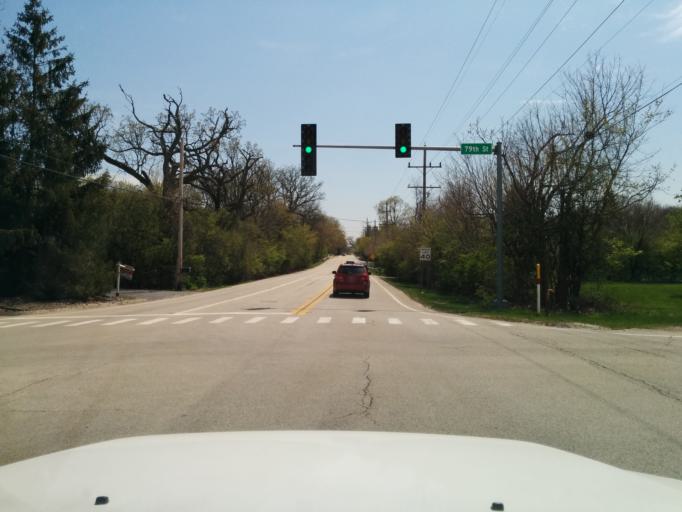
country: US
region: Illinois
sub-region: DuPage County
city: Burr Ridge
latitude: 41.7466
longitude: -87.8962
